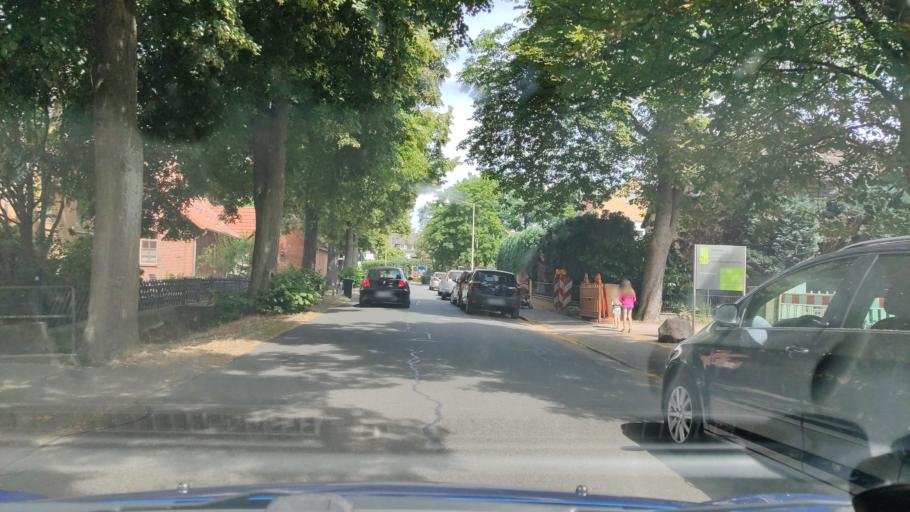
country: DE
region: Lower Saxony
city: Garbsen-Mitte
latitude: 52.4475
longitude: 9.6665
